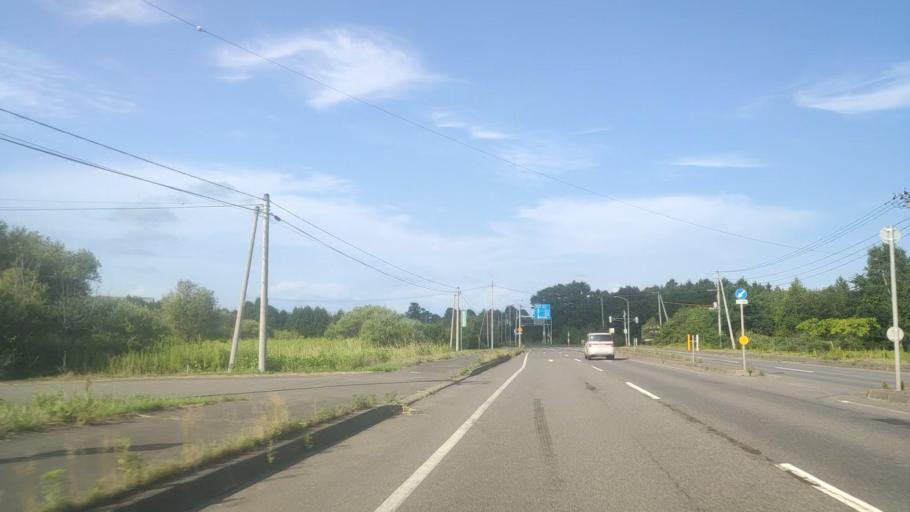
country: JP
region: Hokkaido
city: Chitose
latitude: 42.7763
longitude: 141.8292
